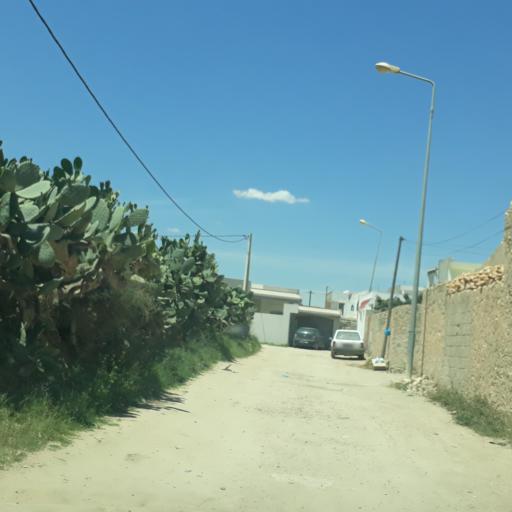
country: TN
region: Safaqis
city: Al Qarmadah
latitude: 34.8157
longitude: 10.7567
